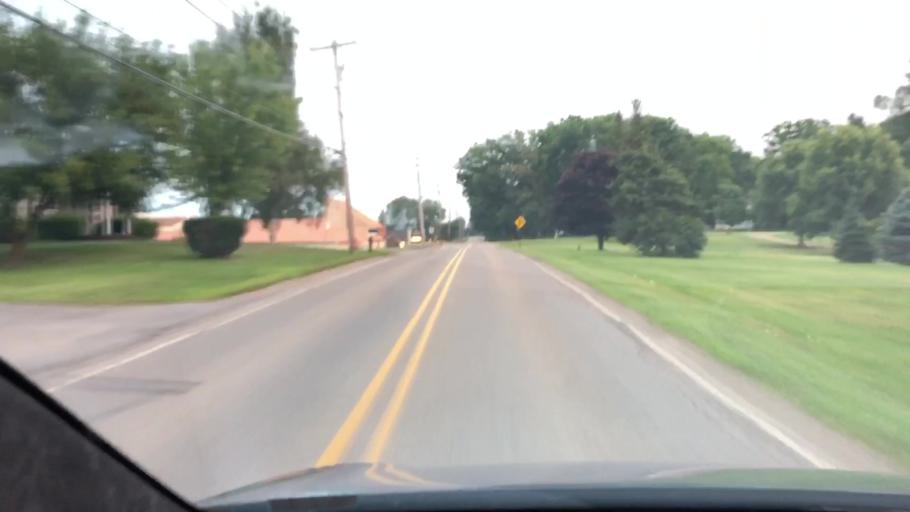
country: US
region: Pennsylvania
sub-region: Butler County
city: Shanor-Northvue
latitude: 40.8946
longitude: -79.9281
